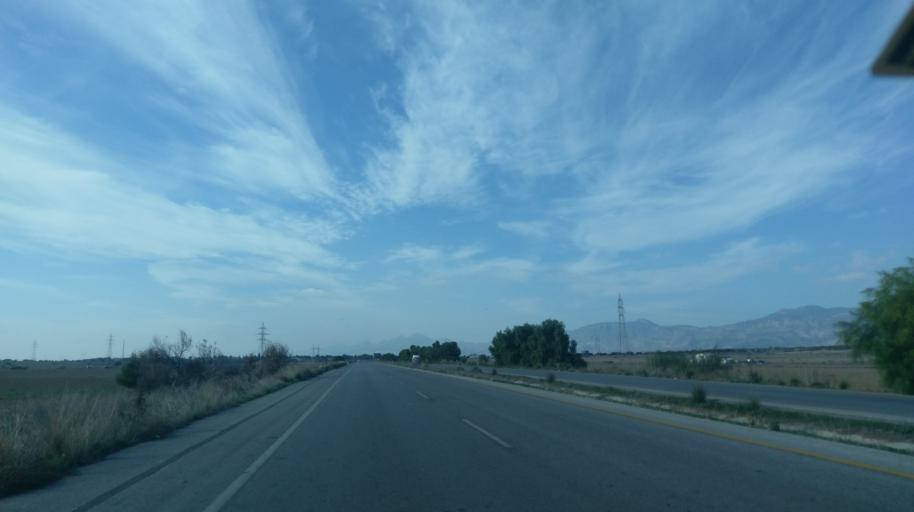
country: CY
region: Ammochostos
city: Lefkonoiko
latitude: 35.1994
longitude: 33.6091
